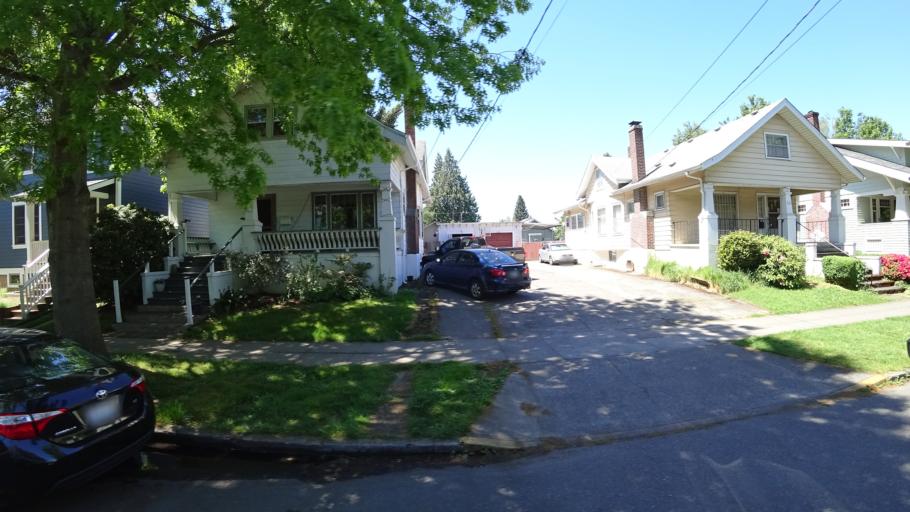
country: US
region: Oregon
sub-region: Multnomah County
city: Portland
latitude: 45.5039
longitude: -122.6305
